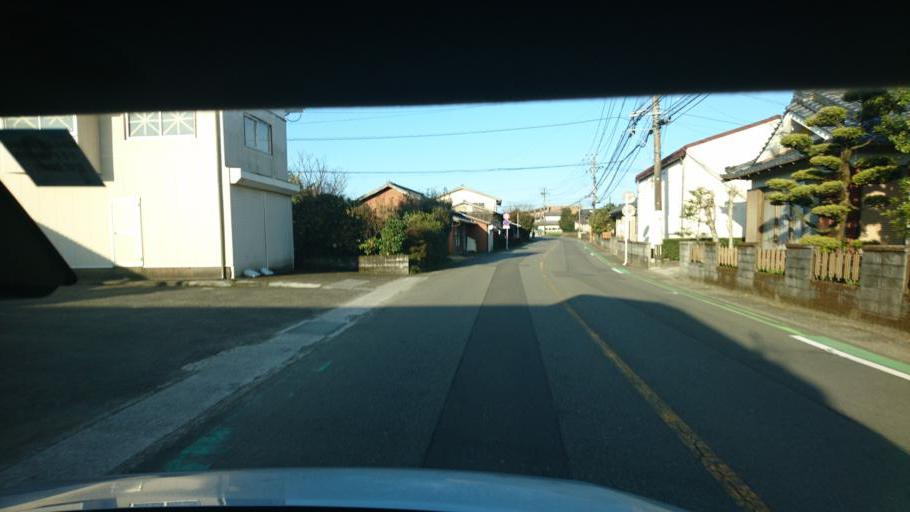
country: JP
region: Miyazaki
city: Miyazaki-shi
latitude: 31.8437
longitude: 131.4041
